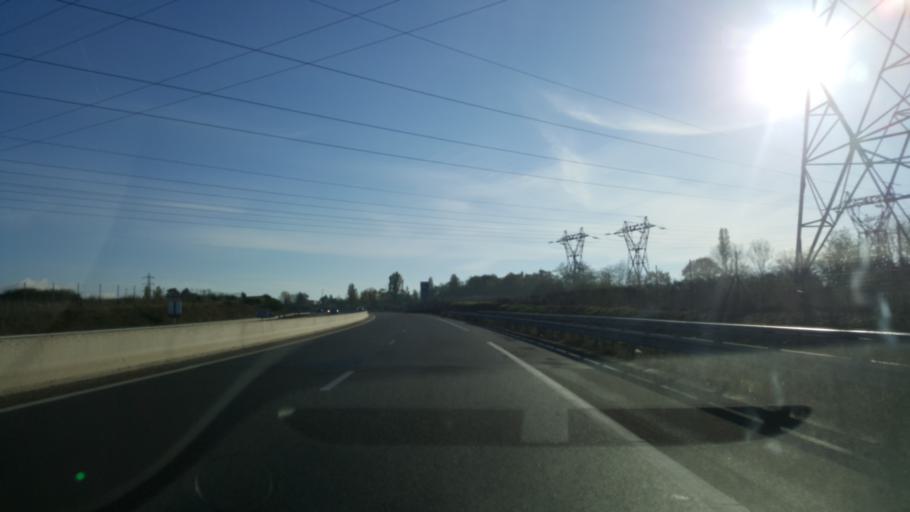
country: FR
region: Rhone-Alpes
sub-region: Departement du Rhone
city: La Tour-de-Salvagny
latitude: 45.8206
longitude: 4.6909
